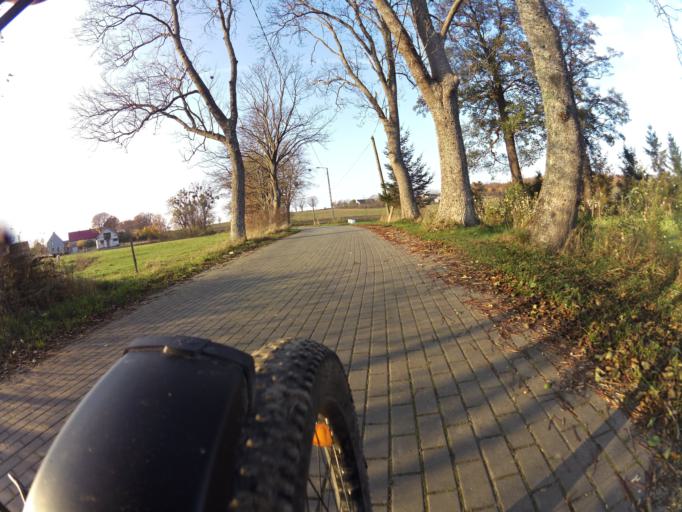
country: PL
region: Pomeranian Voivodeship
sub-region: Powiat pucki
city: Krokowa
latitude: 54.7510
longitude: 18.1889
